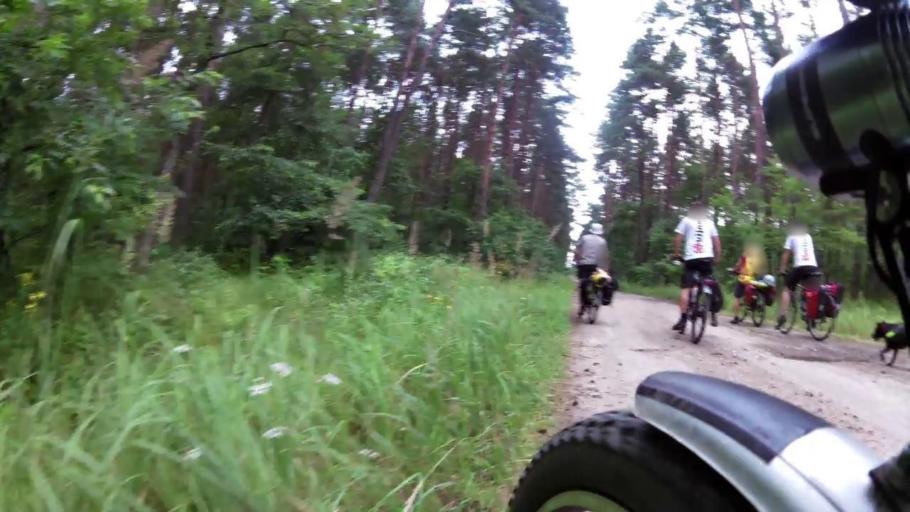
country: PL
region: West Pomeranian Voivodeship
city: Trzcinsko Zdroj
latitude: 52.8568
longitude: 14.6037
